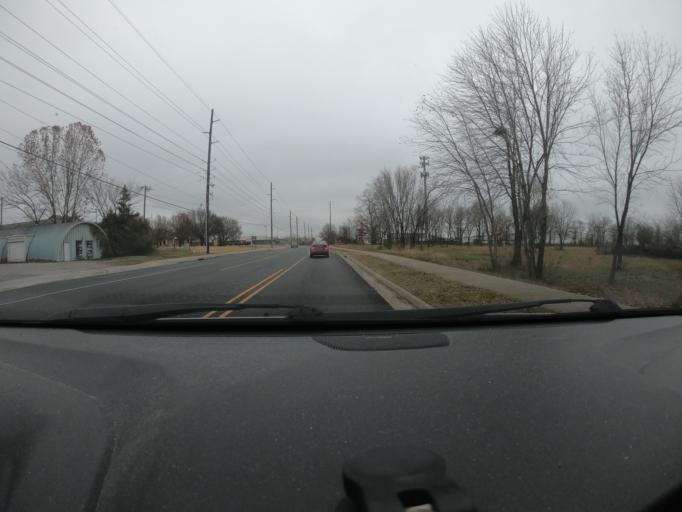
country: US
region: Arkansas
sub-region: Benton County
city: Bentonville
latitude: 36.3640
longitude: -94.2221
